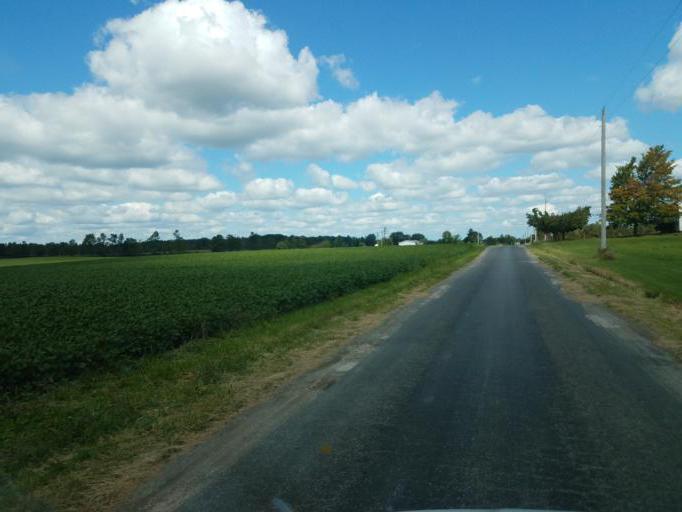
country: US
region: Ohio
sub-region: Wayne County
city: West Salem
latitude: 40.9994
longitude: -82.2027
